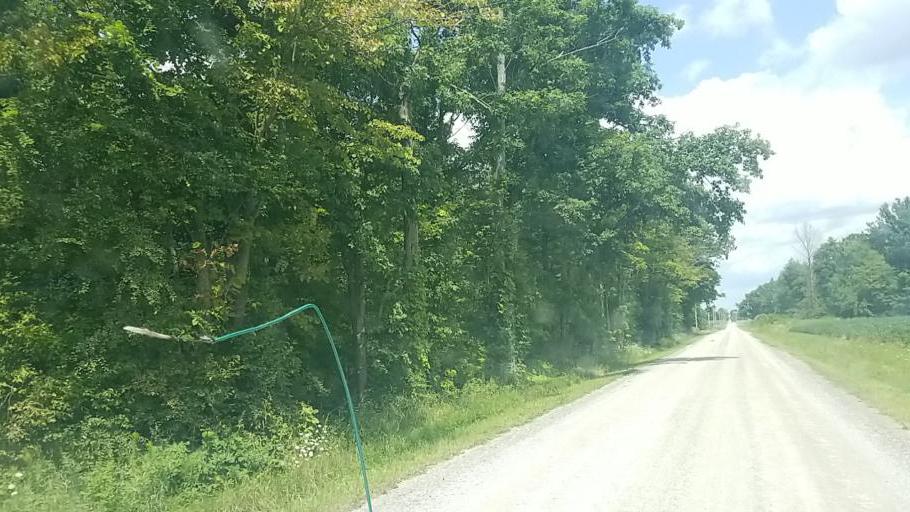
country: US
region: Ohio
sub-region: Wayne County
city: West Salem
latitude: 41.0343
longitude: -82.1451
